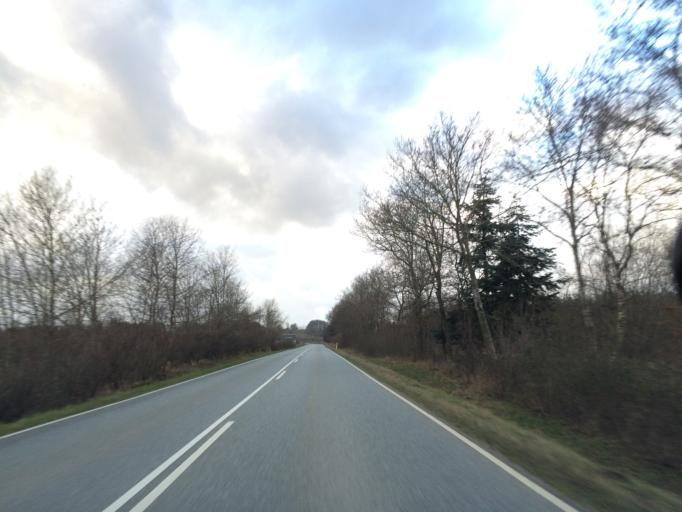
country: DK
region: Central Jutland
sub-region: Silkeborg Kommune
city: Virklund
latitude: 56.1041
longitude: 9.5893
